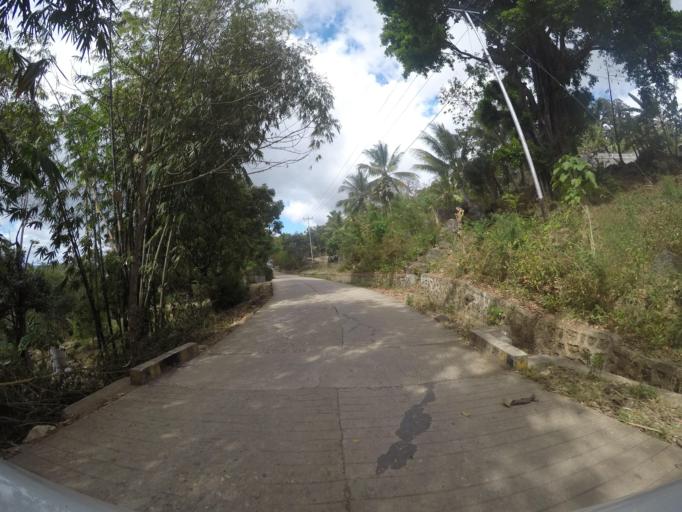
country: TL
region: Lautem
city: Lospalos
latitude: -8.5437
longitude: 126.8310
